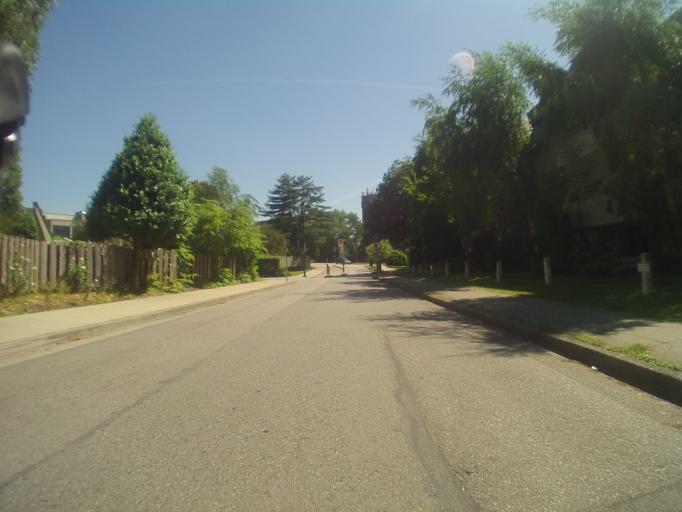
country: CA
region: British Columbia
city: West End
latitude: 49.2734
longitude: -123.1464
